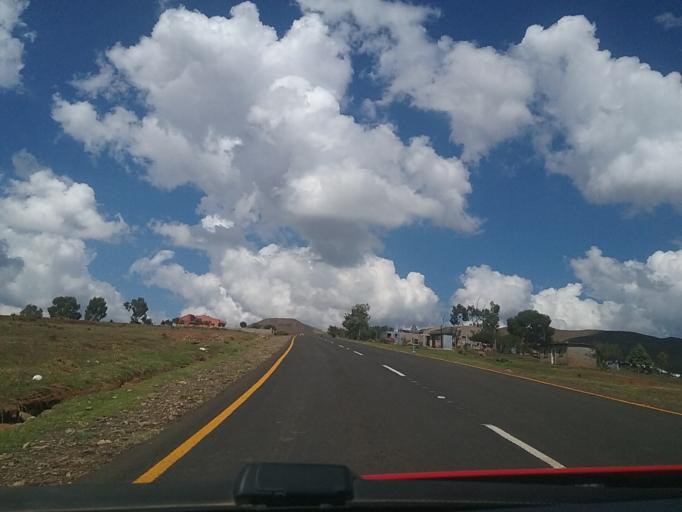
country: LS
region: Berea
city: Teyateyaneng
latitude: -29.2225
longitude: 27.8587
